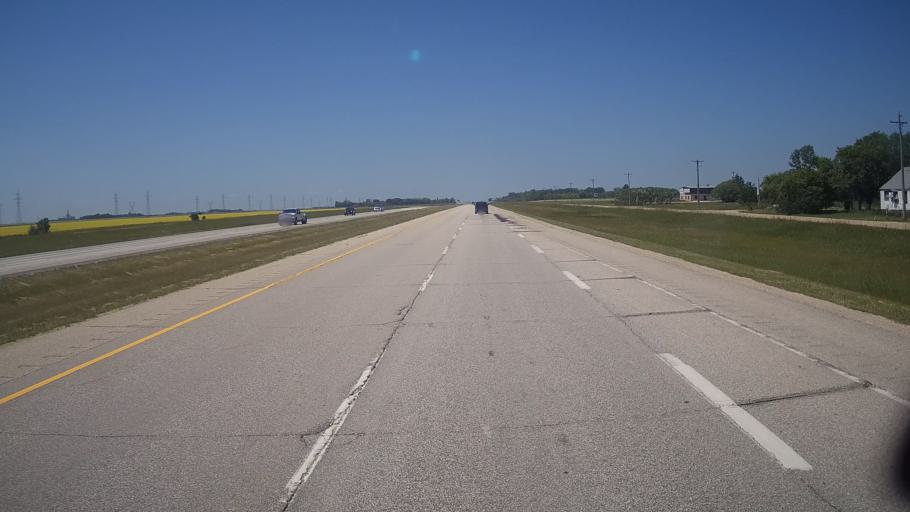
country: CA
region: Manitoba
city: Winnipeg
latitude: 49.9901
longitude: -97.2429
